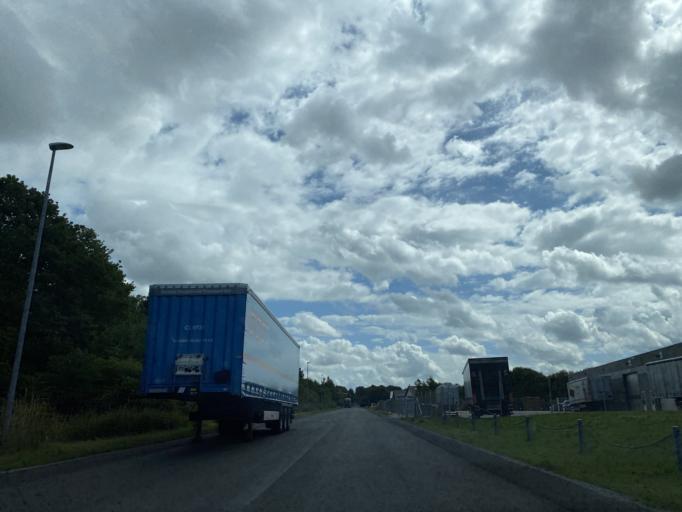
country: DK
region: Central Jutland
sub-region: Silkeborg Kommune
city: Silkeborg
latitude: 56.2070
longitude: 9.5738
